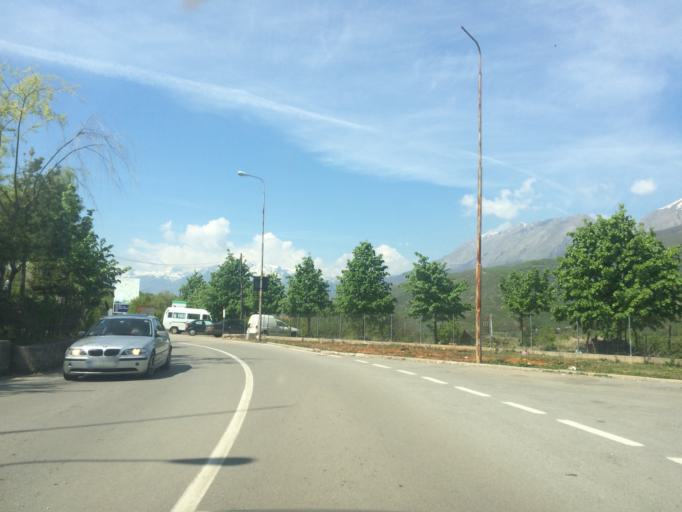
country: XK
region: Gjakova
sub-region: Komuna e Junikut
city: Junik
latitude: 42.4127
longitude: 20.2209
